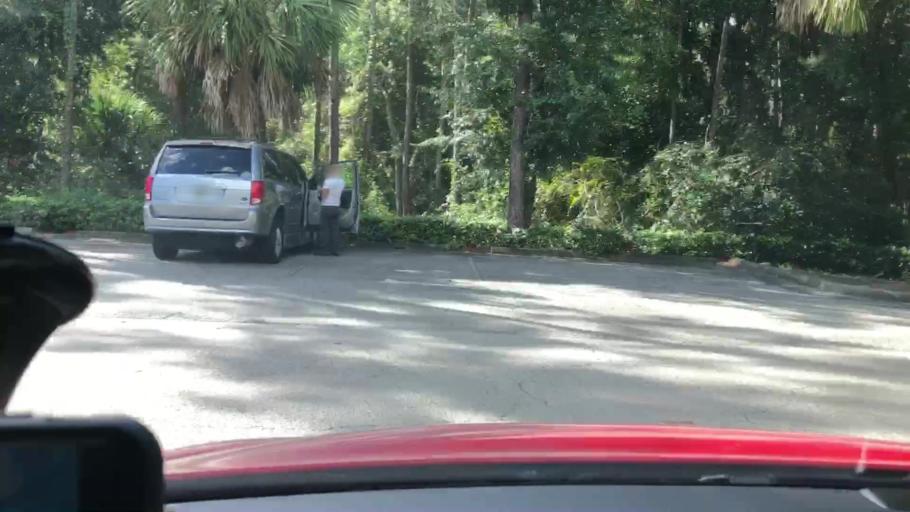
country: US
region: Florida
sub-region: Volusia County
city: Ormond Beach
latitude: 29.2683
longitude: -81.1002
